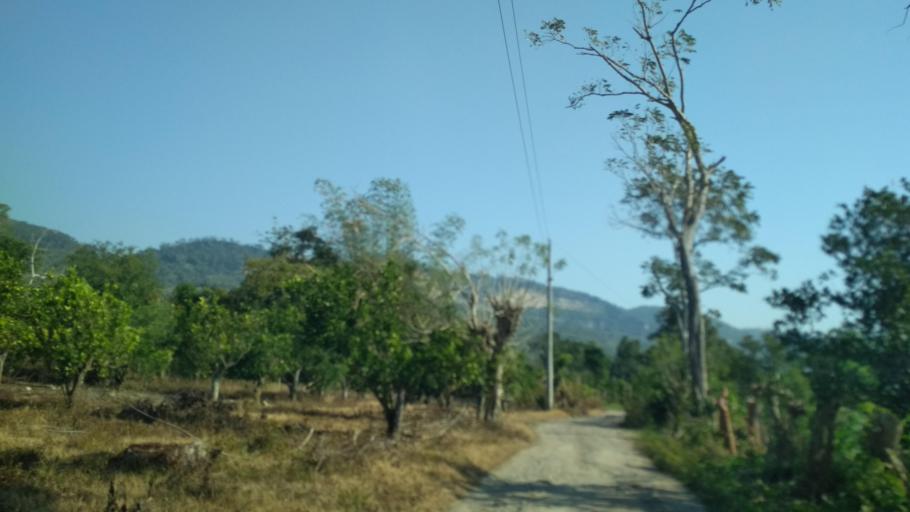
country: MX
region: Veracruz
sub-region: Papantla
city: Polutla
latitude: 20.4573
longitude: -97.2088
